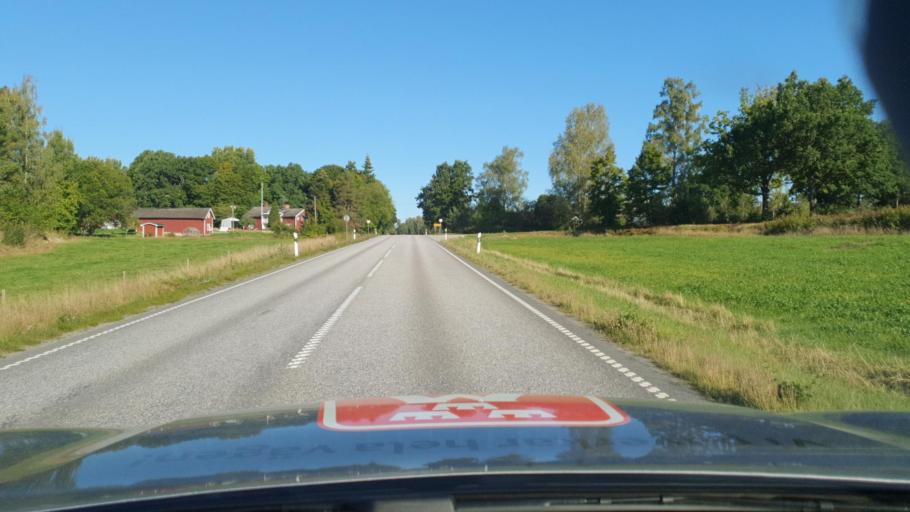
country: SE
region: OEstergoetland
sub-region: Linkopings Kommun
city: Ljungsbro
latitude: 58.7633
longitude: 15.5208
